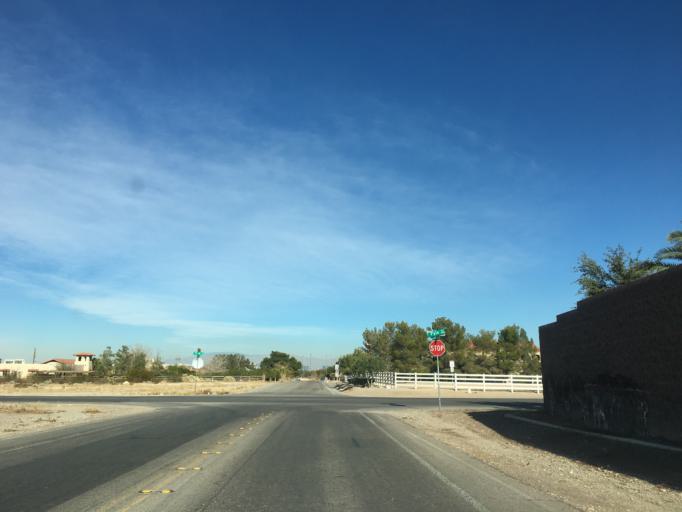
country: US
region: Nevada
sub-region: Clark County
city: Enterprise
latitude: 36.0062
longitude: -115.1658
